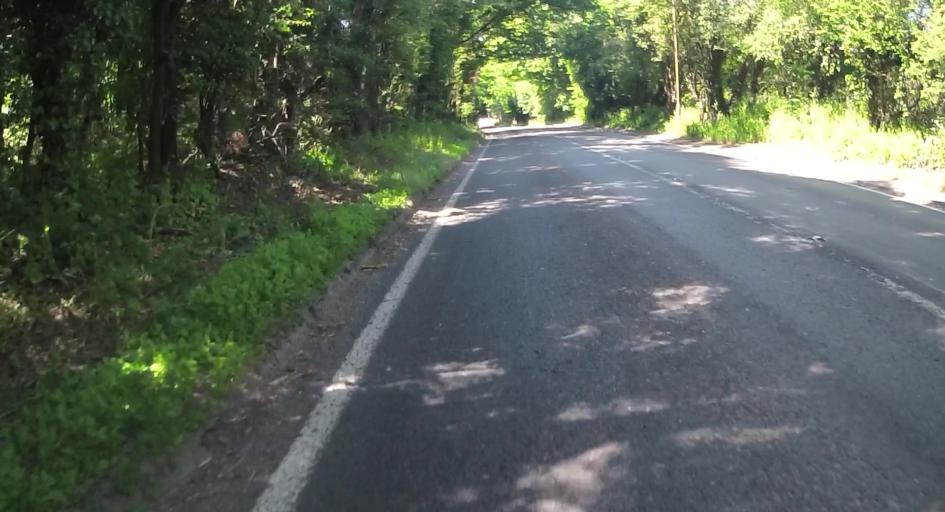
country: GB
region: England
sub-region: West Berkshire
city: Thatcham
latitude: 51.3621
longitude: -1.2650
